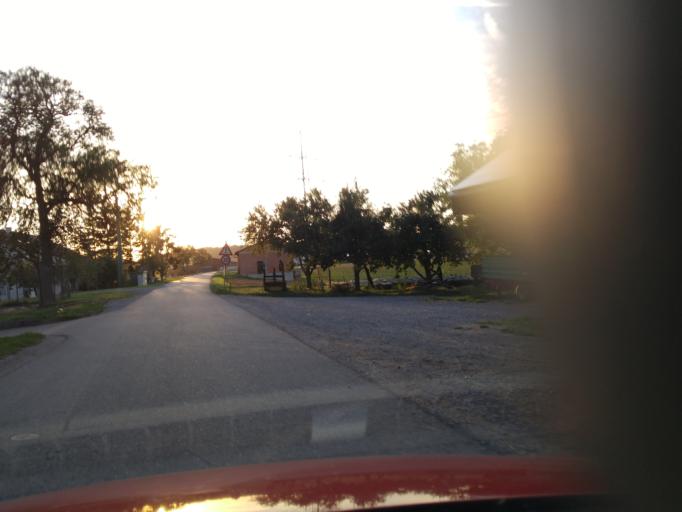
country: DE
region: Baden-Wuerttemberg
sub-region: Regierungsbezirk Stuttgart
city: Untereisesheim
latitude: 49.2011
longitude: 9.1878
